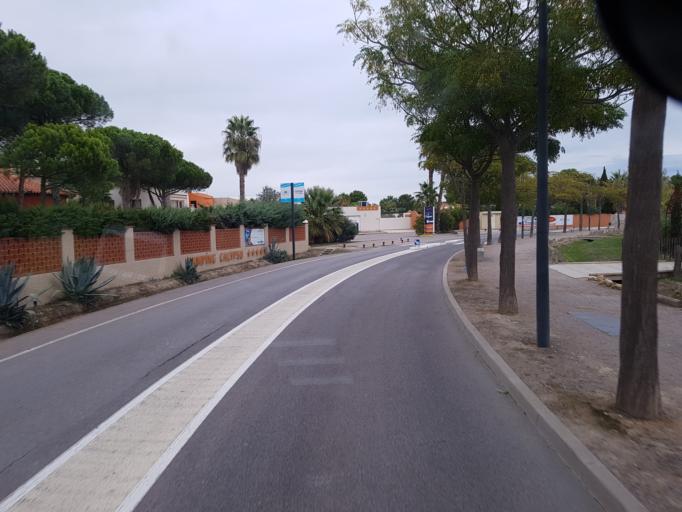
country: FR
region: Languedoc-Roussillon
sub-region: Departement des Pyrenees-Orientales
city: Le Barcares
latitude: 42.7670
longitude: 3.0281
